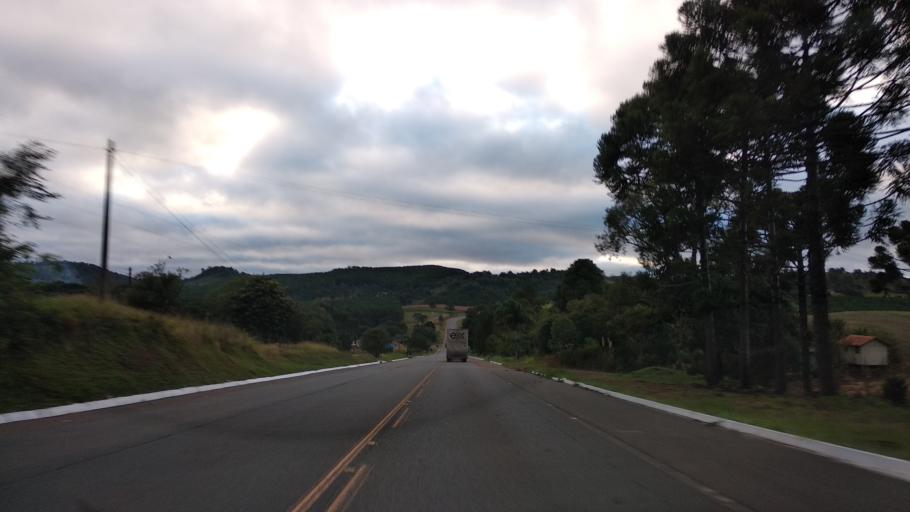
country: BR
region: Santa Catarina
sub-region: Campos Novos
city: Campos Novos
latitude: -27.4954
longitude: -50.9616
